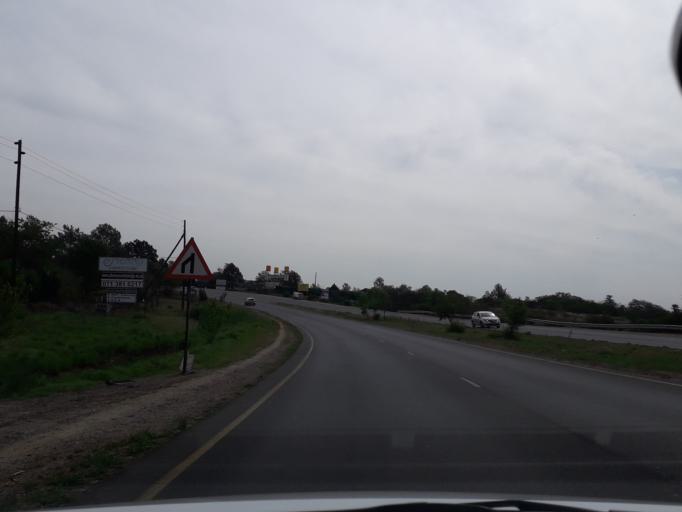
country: ZA
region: Gauteng
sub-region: City of Johannesburg Metropolitan Municipality
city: Diepsloot
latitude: -25.9873
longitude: 28.0553
